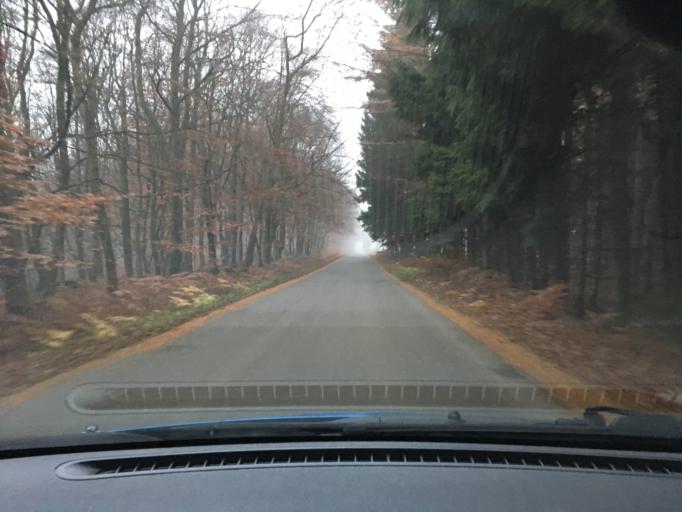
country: DE
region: Lower Saxony
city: Oldendorf
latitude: 53.1527
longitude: 10.1825
